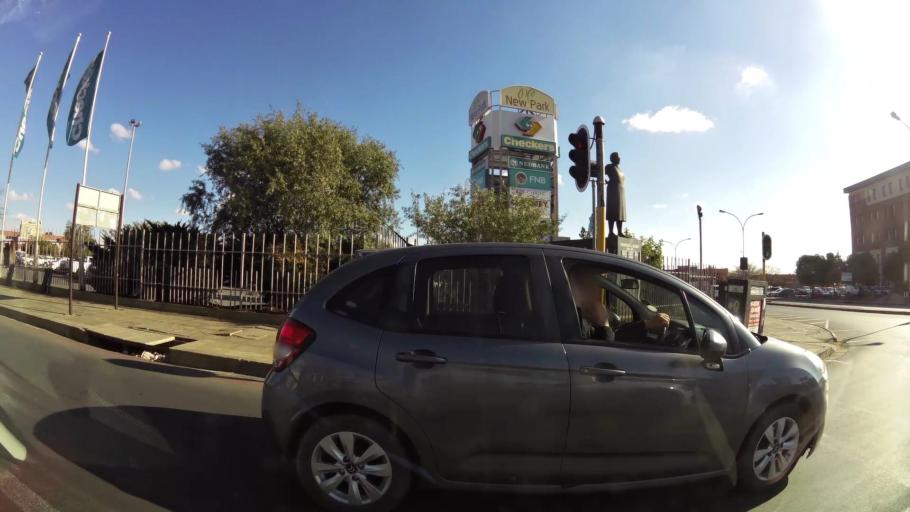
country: ZA
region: Northern Cape
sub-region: Frances Baard District Municipality
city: Kimberley
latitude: -28.7437
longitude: 24.7626
